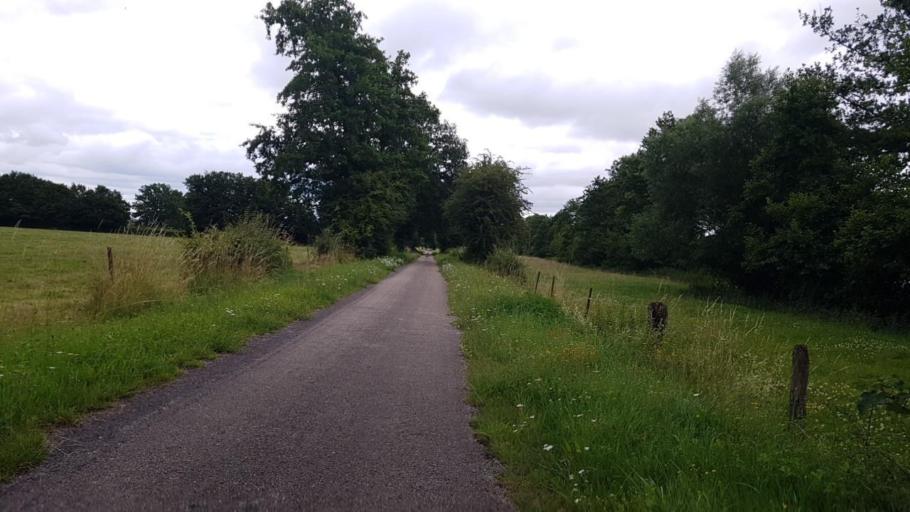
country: FR
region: Picardie
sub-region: Departement de l'Aisne
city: Buironfosse
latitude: 49.9041
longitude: 3.8008
